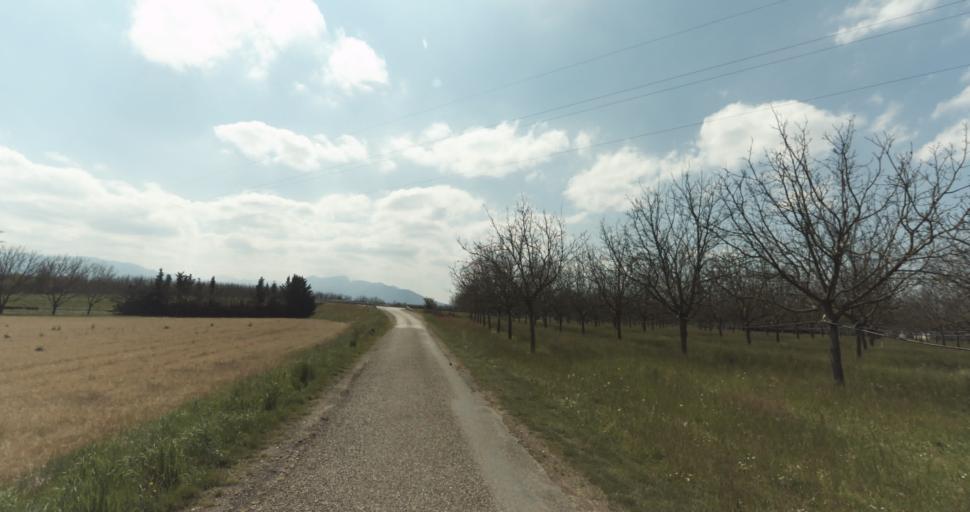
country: FR
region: Rhone-Alpes
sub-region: Departement de l'Isere
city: Saint-Marcellin
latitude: 45.1340
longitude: 5.3146
